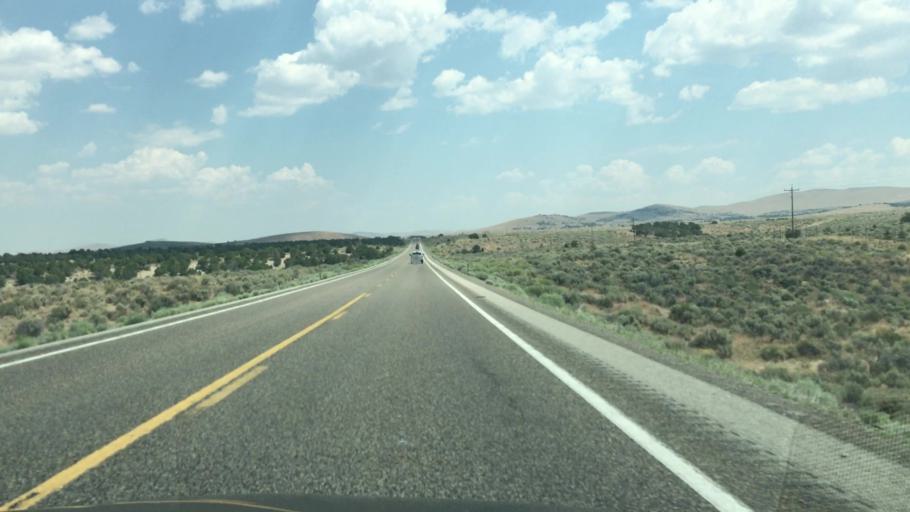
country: US
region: Nevada
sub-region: Elko County
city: Wells
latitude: 41.1961
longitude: -114.8633
